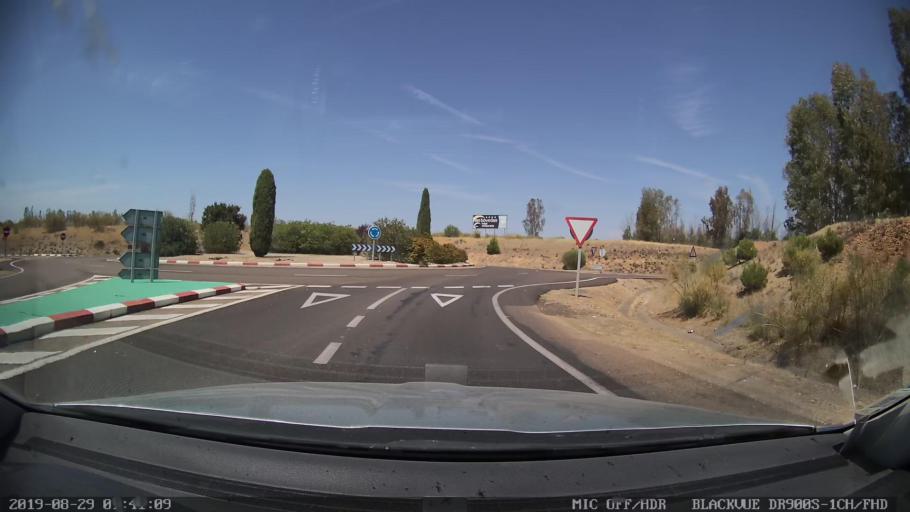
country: ES
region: Extremadura
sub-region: Provincia de Badajoz
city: Badajoz
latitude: 38.8863
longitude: -7.0262
